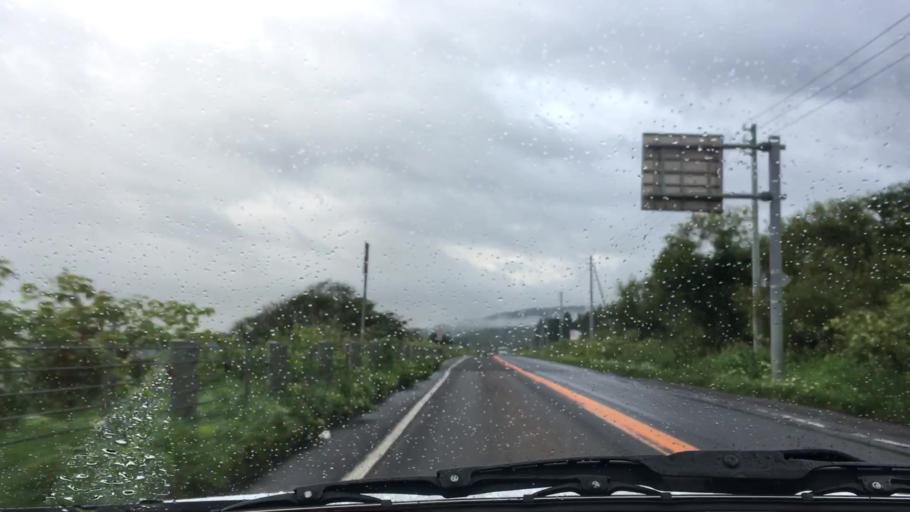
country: JP
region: Hokkaido
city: Nanae
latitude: 42.1855
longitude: 140.4369
